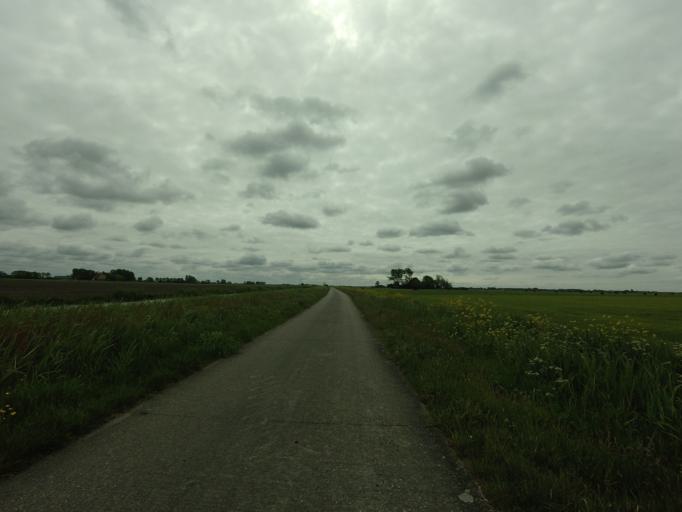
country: NL
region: Friesland
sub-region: Sudwest Fryslan
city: Workum
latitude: 52.9496
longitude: 5.4545
